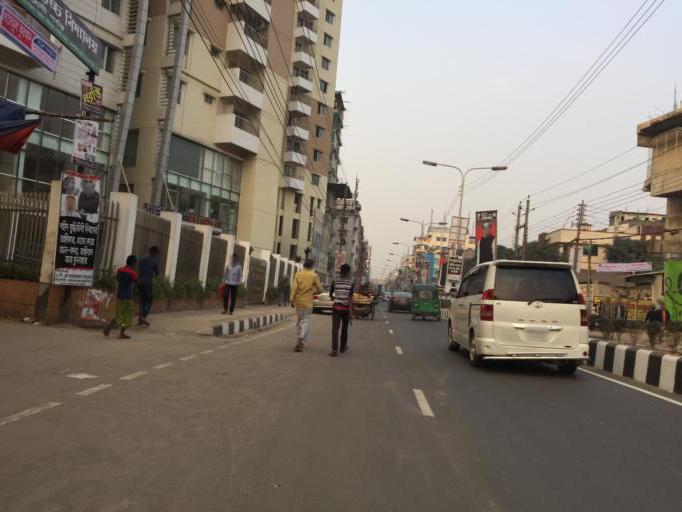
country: BD
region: Dhaka
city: Azimpur
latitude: 23.7893
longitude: 90.3481
